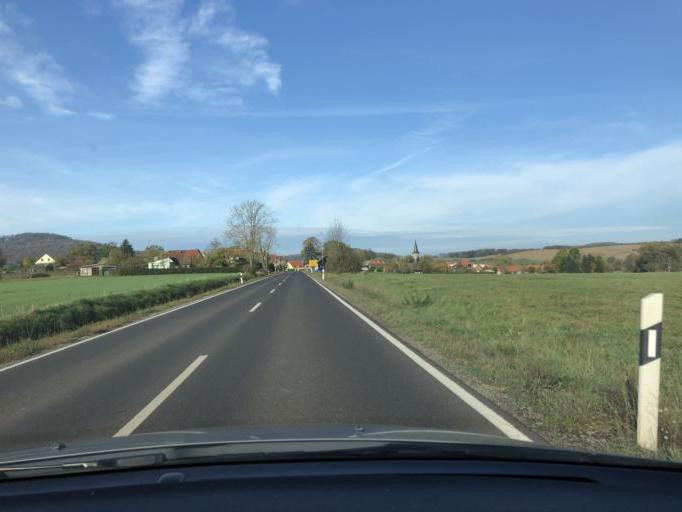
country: DE
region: Thuringia
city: Reurieth
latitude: 50.4111
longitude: 10.6387
